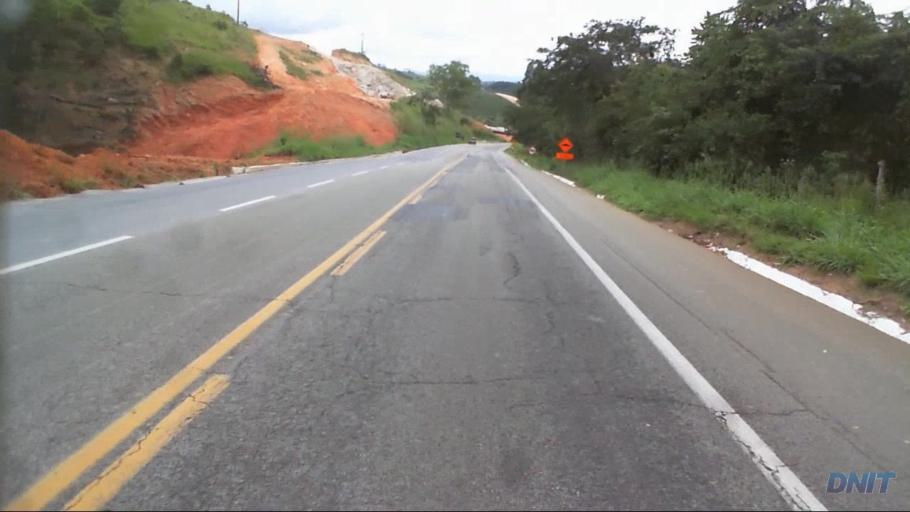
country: BR
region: Minas Gerais
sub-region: Barao De Cocais
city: Barao de Cocais
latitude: -19.7924
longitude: -43.4274
